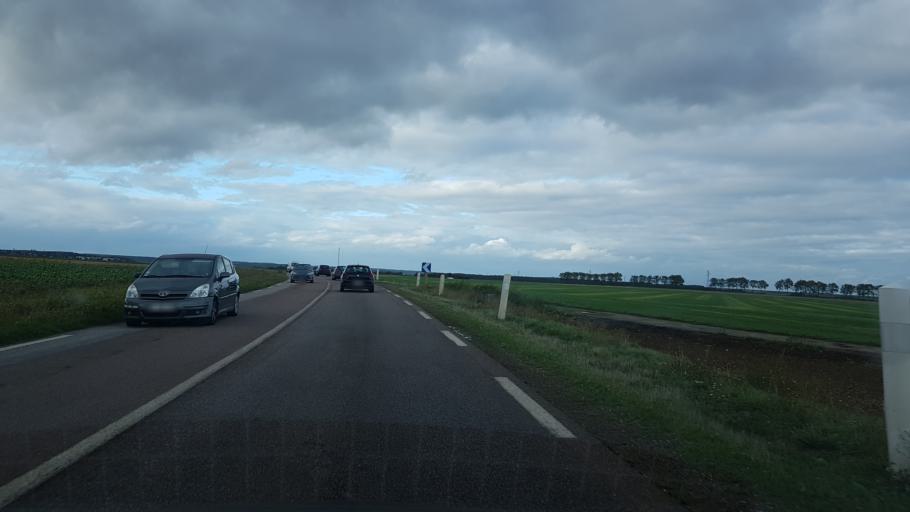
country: FR
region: Ile-de-France
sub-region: Departement de l'Essonne
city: Morigny-Champigny
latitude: 48.4113
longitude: 2.1794
